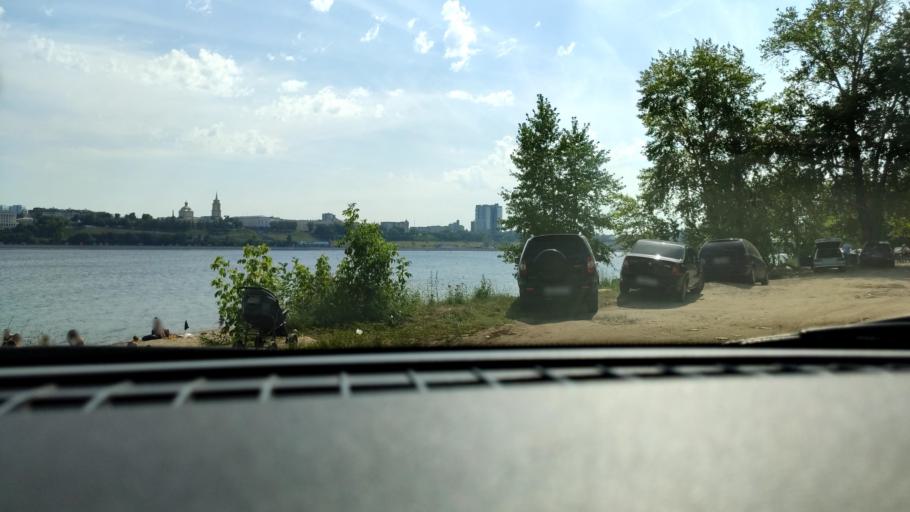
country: RU
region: Perm
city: Perm
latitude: 58.0280
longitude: 56.2383
